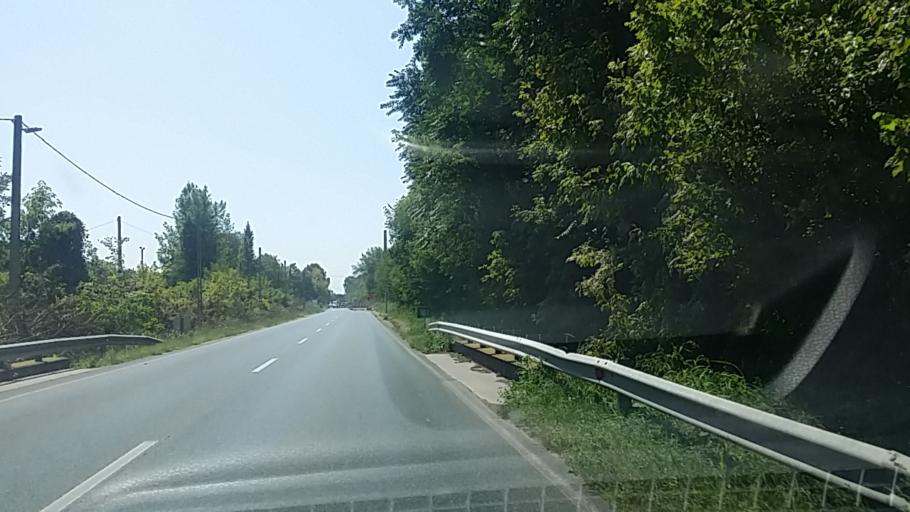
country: HU
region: Tolna
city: Paks
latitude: 46.6432
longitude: 18.8792
